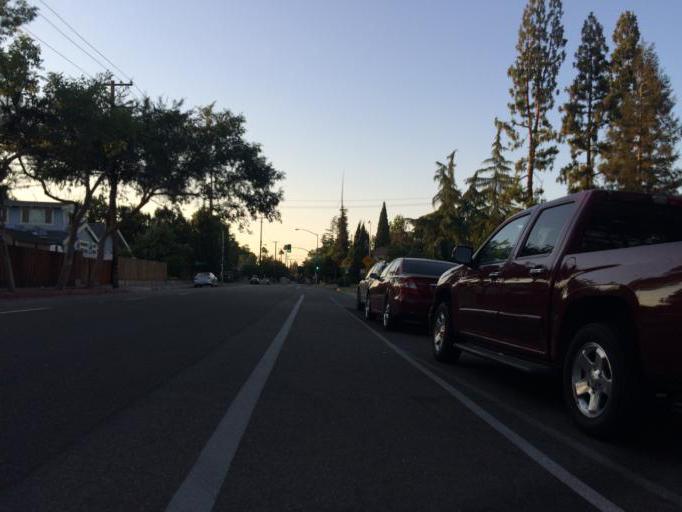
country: US
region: California
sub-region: Fresno County
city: Fresno
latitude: 36.7677
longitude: -119.7995
